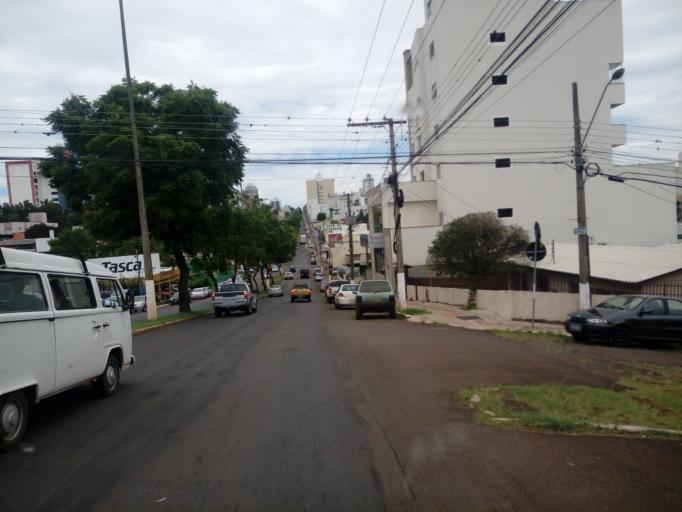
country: BR
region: Santa Catarina
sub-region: Chapeco
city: Chapeco
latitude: -27.0990
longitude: -52.6211
